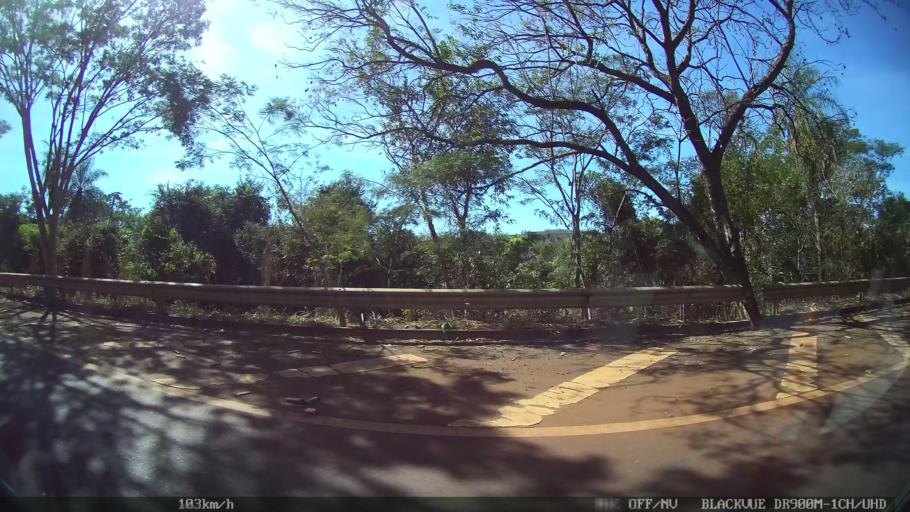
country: BR
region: Sao Paulo
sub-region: Sao Joaquim Da Barra
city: Sao Joaquim da Barra
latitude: -20.5303
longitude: -47.8323
